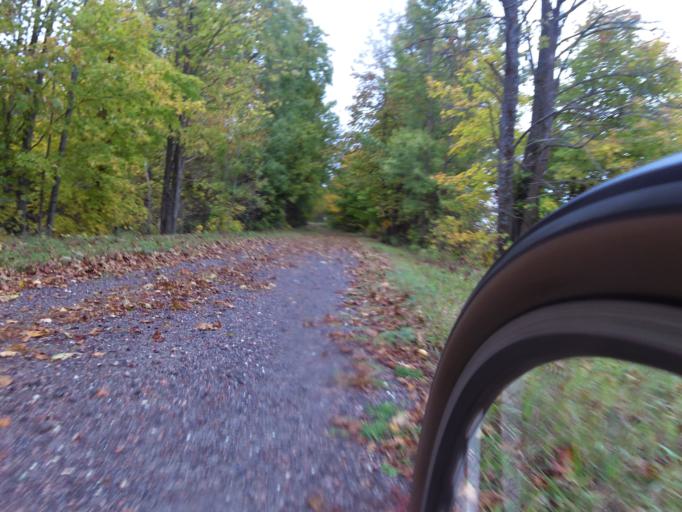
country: CA
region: Quebec
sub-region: Outaouais
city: Shawville
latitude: 45.6419
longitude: -76.5186
